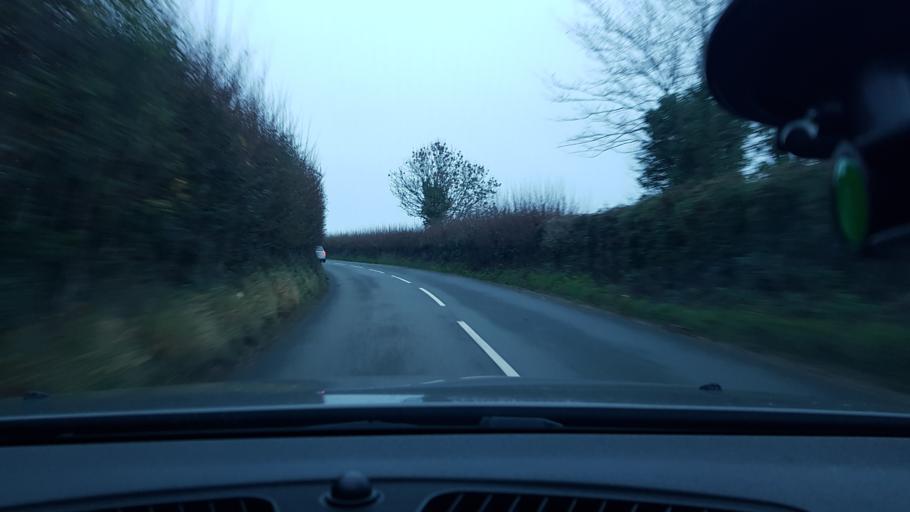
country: GB
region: England
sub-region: Dorset
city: Bovington Camp
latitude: 50.7471
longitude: -2.2693
